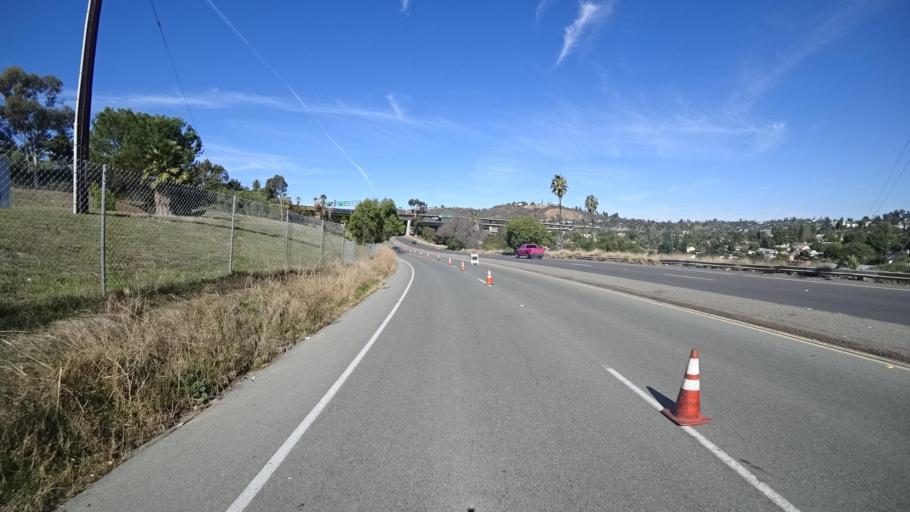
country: US
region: California
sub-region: San Diego County
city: Spring Valley
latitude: 32.7414
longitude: -117.0149
